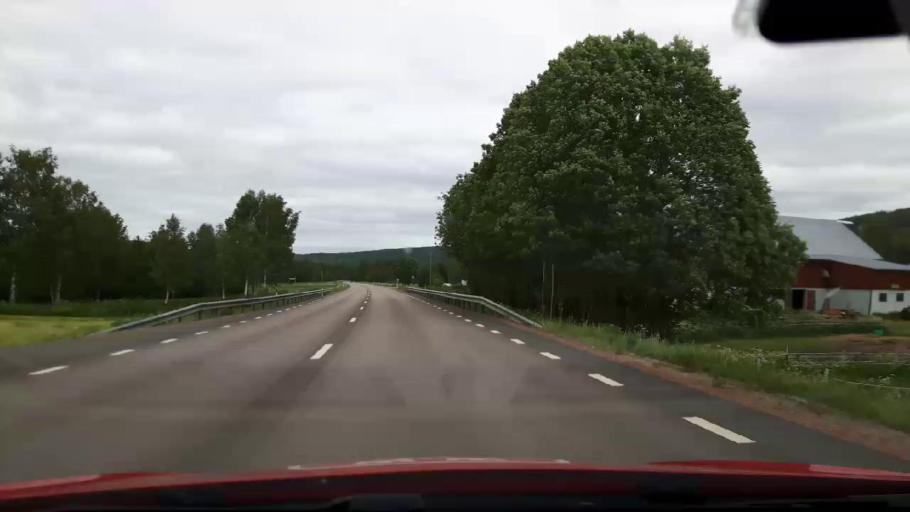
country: SE
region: Jaemtland
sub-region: Ragunda Kommun
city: Hammarstrand
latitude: 63.1502
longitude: 16.2673
